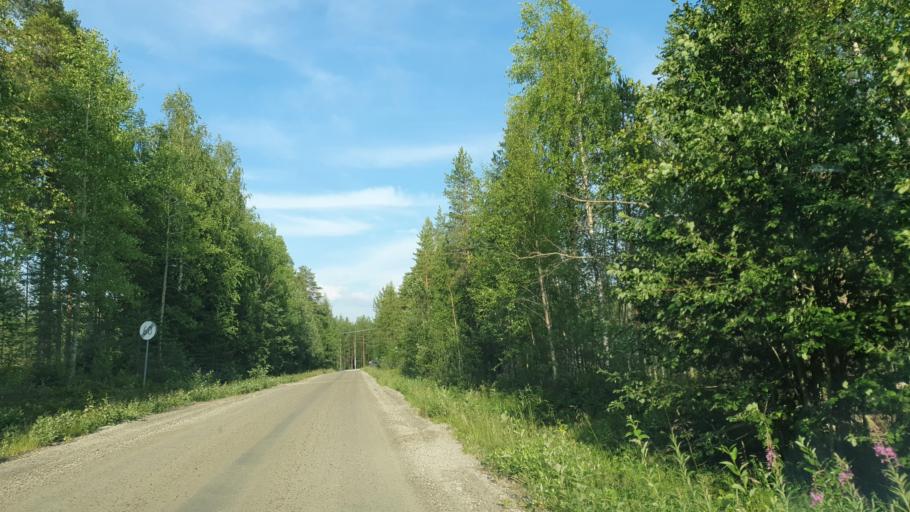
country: FI
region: Kainuu
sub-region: Kehys-Kainuu
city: Kuhmo
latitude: 64.2668
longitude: 29.8163
